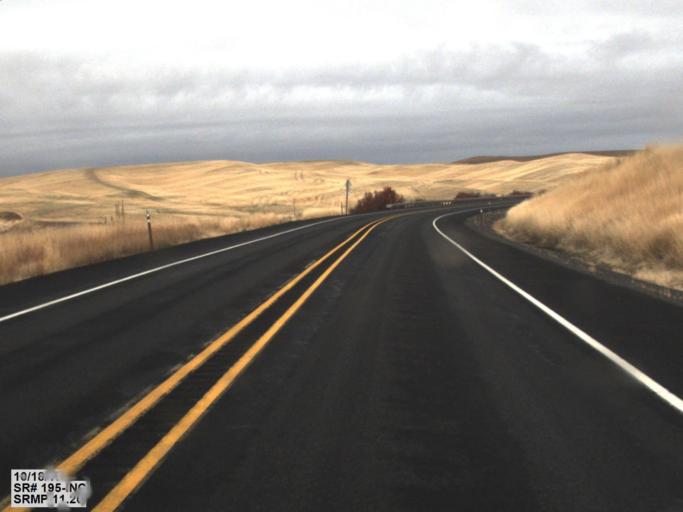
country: US
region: Washington
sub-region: Whitman County
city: Pullman
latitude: 46.5945
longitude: -117.1734
